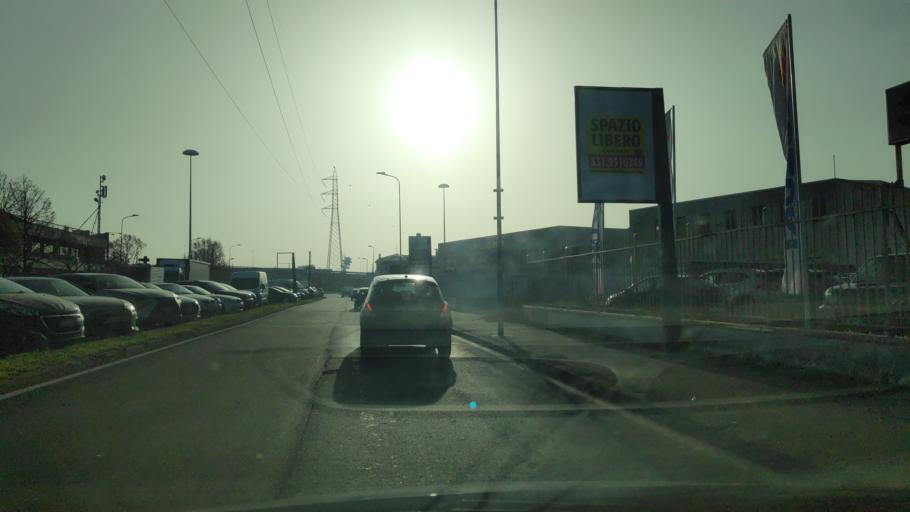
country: IT
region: Lombardy
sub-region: Citta metropolitana di Milano
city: Rozzano
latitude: 45.3899
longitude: 9.1697
